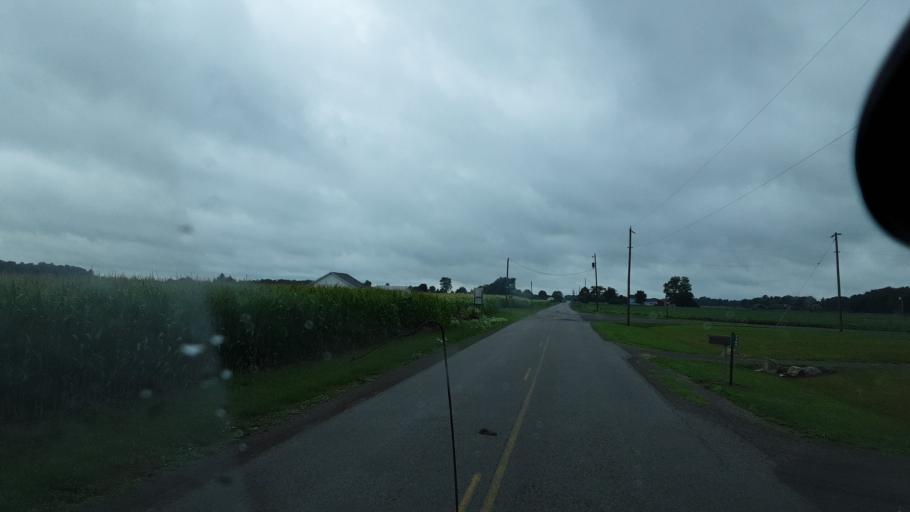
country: US
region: Ohio
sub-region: Van Wert County
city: Convoy
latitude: 40.8005
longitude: -84.6860
